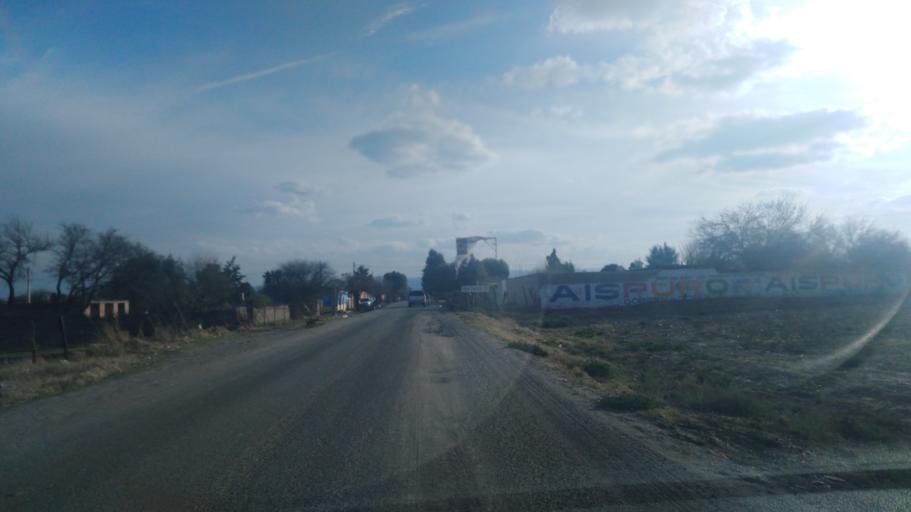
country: MX
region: Durango
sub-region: Durango
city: Jose Refugio Salcido
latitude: 23.9963
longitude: -104.4782
